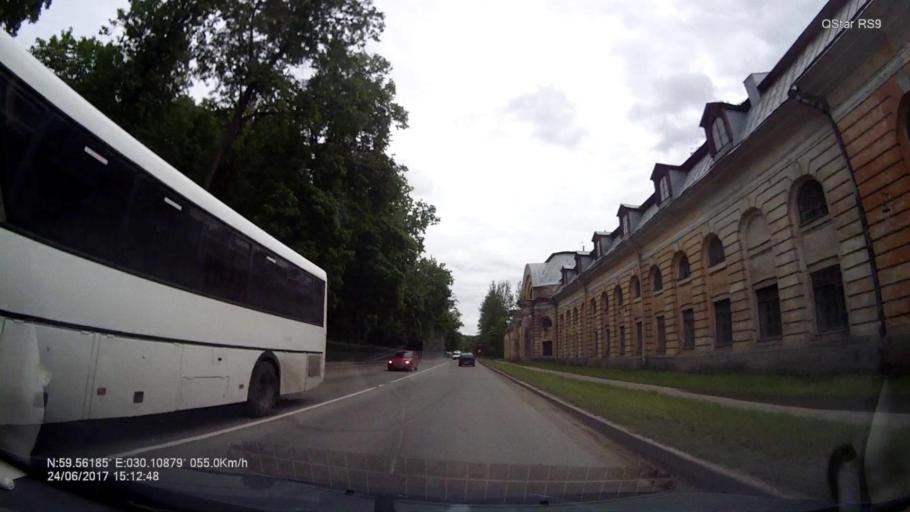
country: RU
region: Leningrad
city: Gatchina
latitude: 59.5617
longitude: 30.1091
